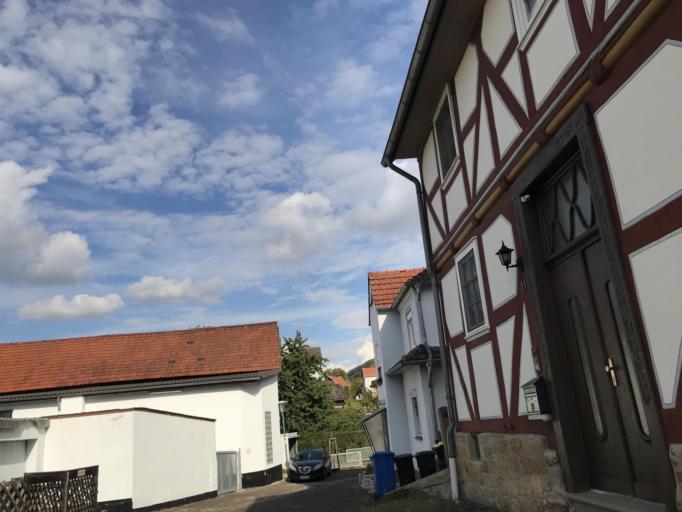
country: DE
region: Hesse
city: Felsberg
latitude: 51.1281
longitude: 9.4361
